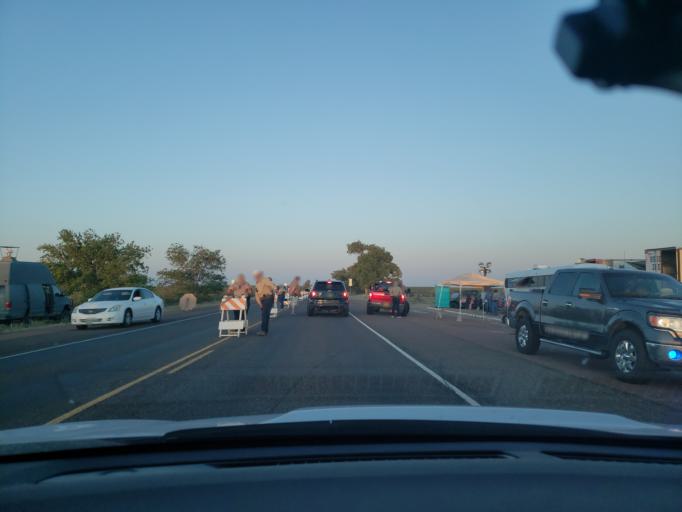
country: US
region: Texas
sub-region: Hudspeth County
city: Sierra Blanca
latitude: 31.7613
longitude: -105.3673
